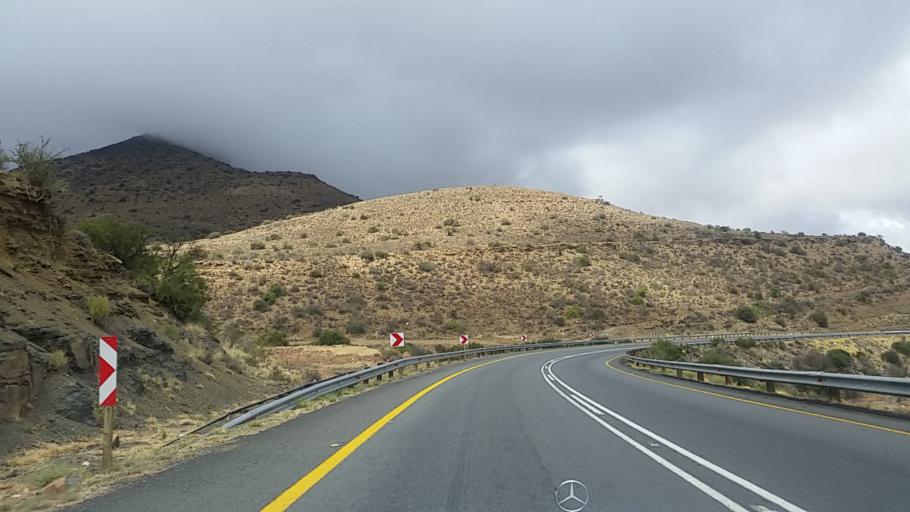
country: ZA
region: Eastern Cape
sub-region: Cacadu District Municipality
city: Graaff-Reinet
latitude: -32.1109
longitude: 24.6096
